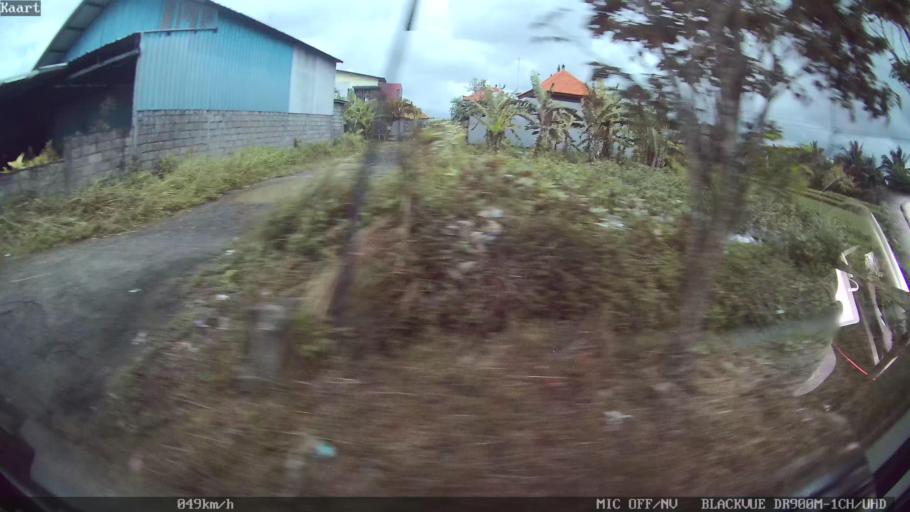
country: ID
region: Bali
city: Banjar Serangan
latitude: -8.5337
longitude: 115.1786
